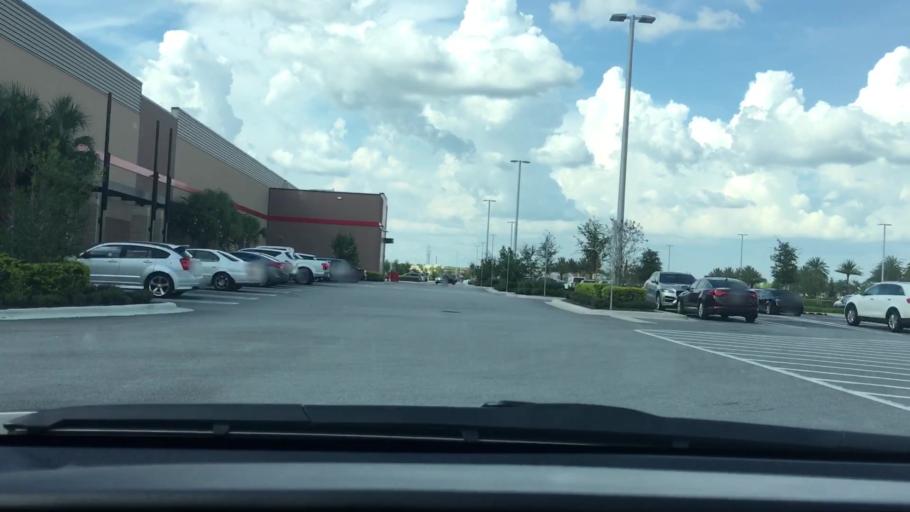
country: US
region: Florida
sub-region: Hillsborough County
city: Pebble Creek
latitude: 28.1882
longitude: -82.3936
